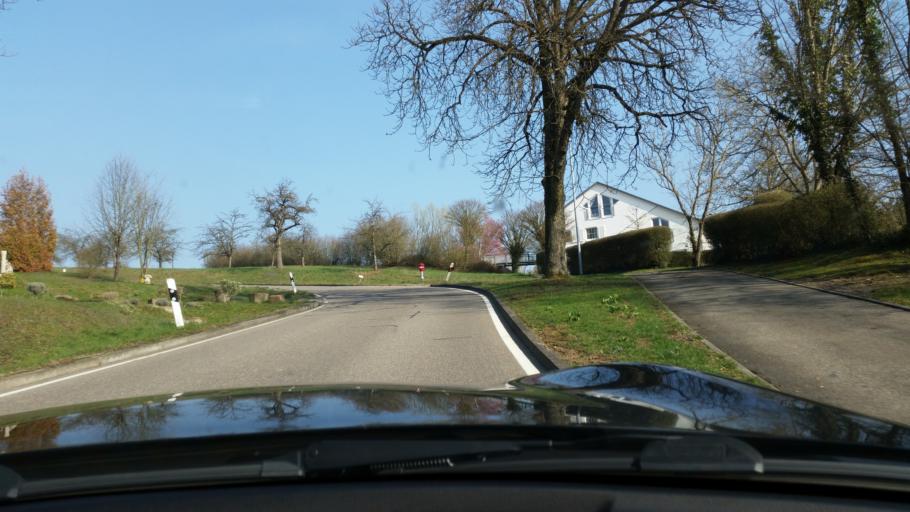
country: DE
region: Baden-Wuerttemberg
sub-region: Regierungsbezirk Stuttgart
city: Mockmuhl
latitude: 49.3275
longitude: 9.3598
